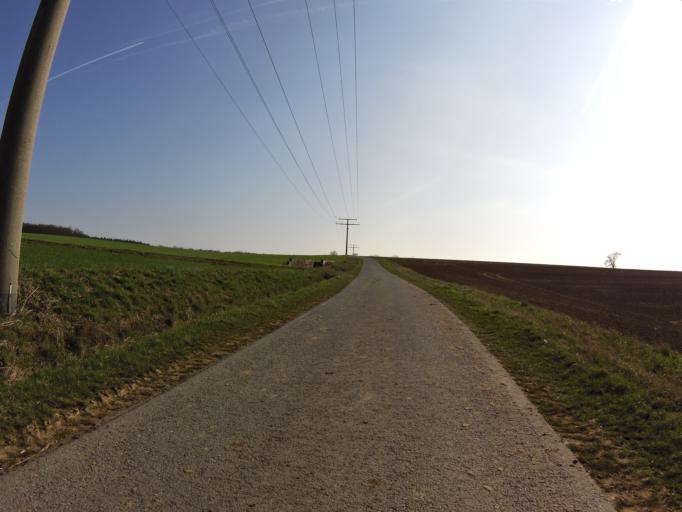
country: DE
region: Bavaria
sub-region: Regierungsbezirk Unterfranken
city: Rottendorf
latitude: 49.8209
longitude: 10.0300
